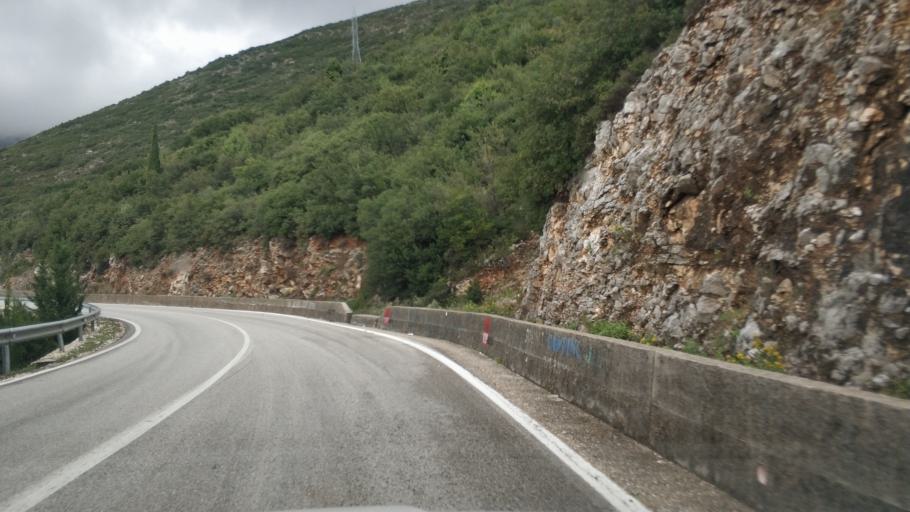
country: AL
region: Vlore
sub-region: Rrethi i Vlores
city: Vranisht
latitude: 40.1421
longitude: 19.6871
